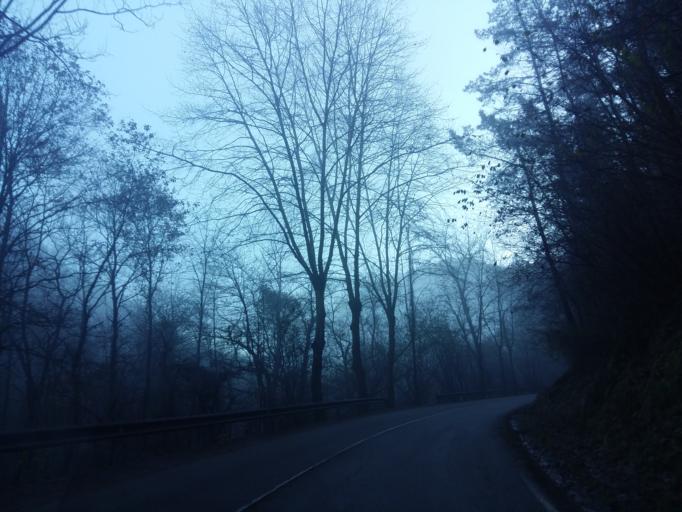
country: ES
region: Cantabria
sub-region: Provincia de Cantabria
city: Arredondo
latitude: 43.2769
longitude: -3.5793
